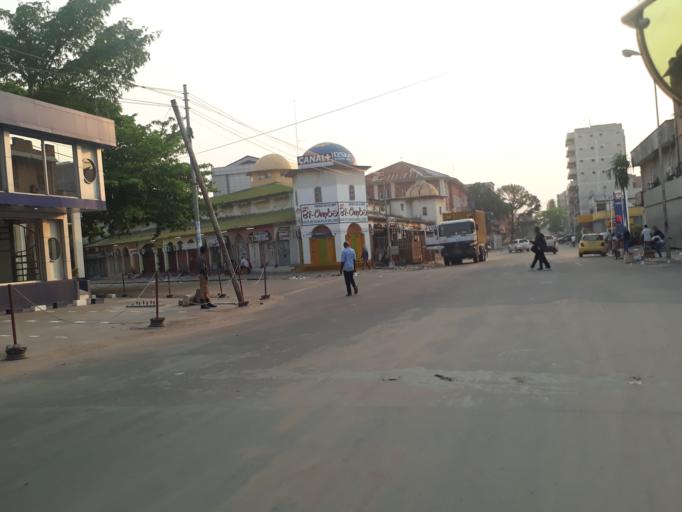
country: CD
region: Kinshasa
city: Kinshasa
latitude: -4.3056
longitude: 15.3097
